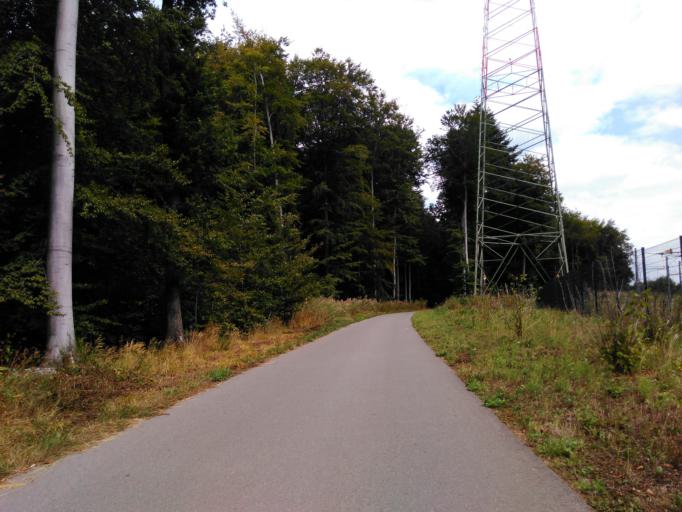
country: LU
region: Luxembourg
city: Kirchberg
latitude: 49.6386
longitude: 6.1822
